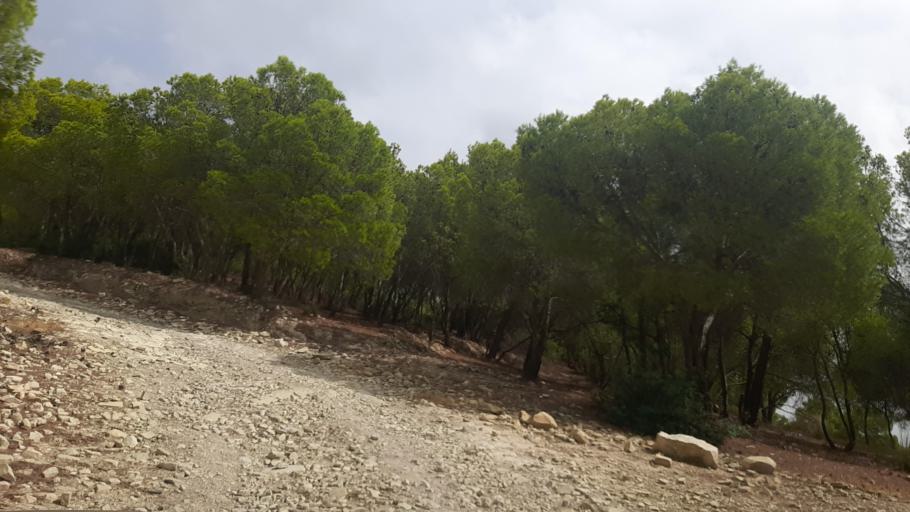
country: TN
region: Zaghwan
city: El Fahs
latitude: 36.1958
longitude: 9.8439
